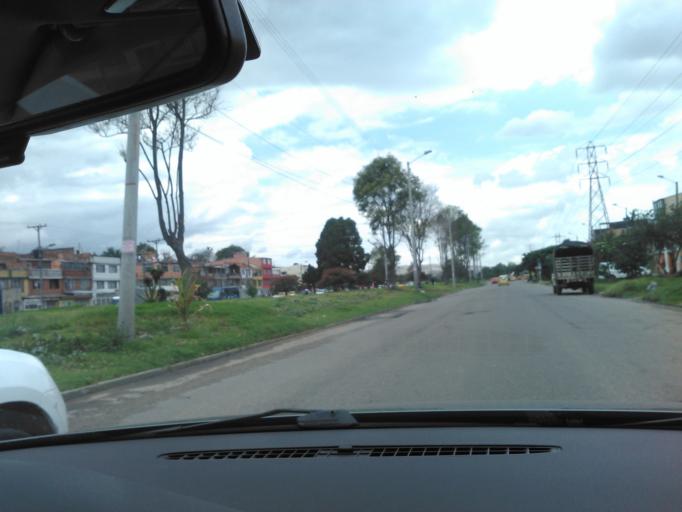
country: CO
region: Bogota D.C.
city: Bogota
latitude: 4.6162
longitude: -74.1120
